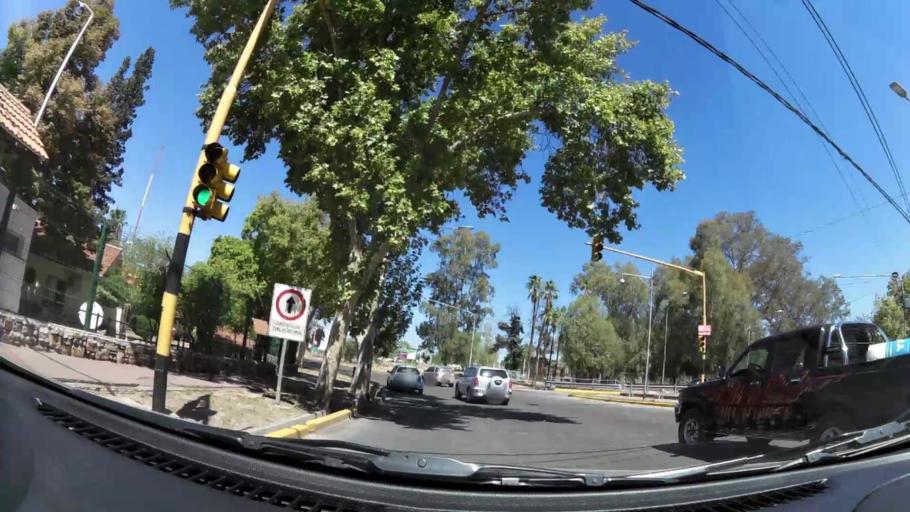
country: AR
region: Mendoza
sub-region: Departamento de Godoy Cruz
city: Godoy Cruz
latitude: -32.9027
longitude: -68.8671
